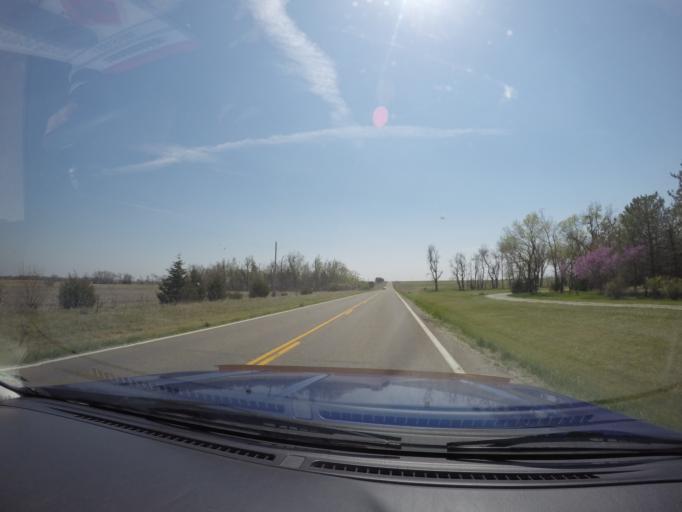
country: US
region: Kansas
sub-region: Morris County
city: Council Grove
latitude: 38.8027
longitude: -96.5013
